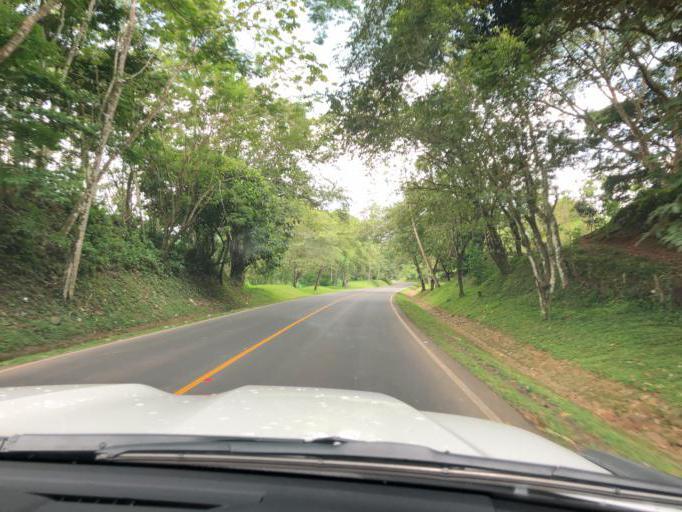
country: NI
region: Chontales
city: Villa Sandino
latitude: 11.9945
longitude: -84.8286
